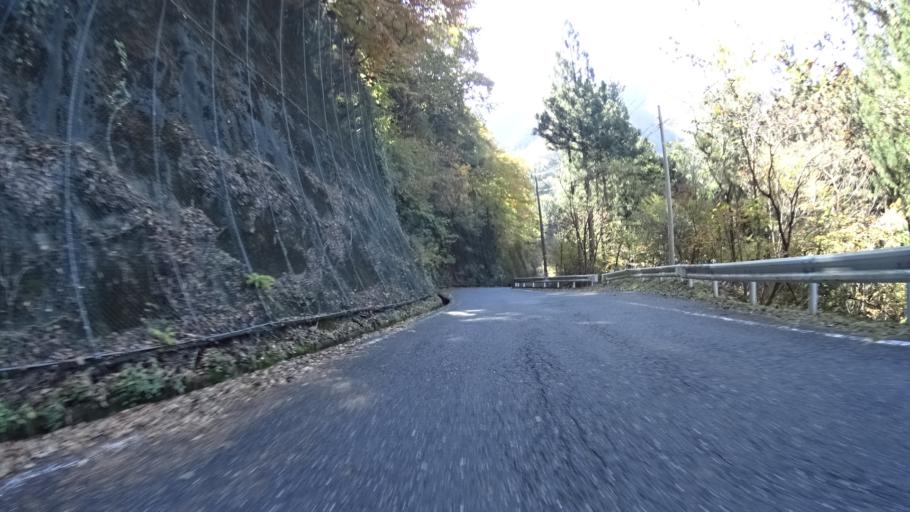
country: JP
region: Yamanashi
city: Otsuki
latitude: 35.7798
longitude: 138.9219
